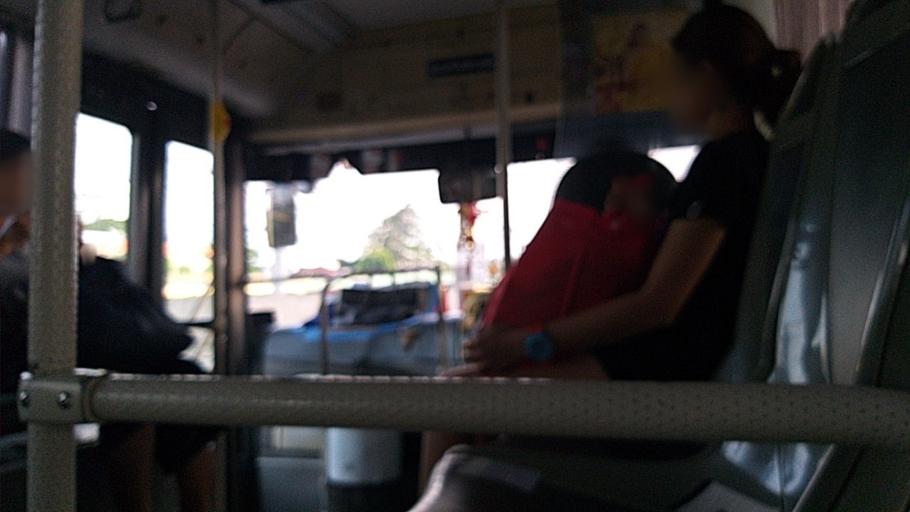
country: TH
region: Bangkok
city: Sai Mai
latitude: 13.9770
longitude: 100.6183
